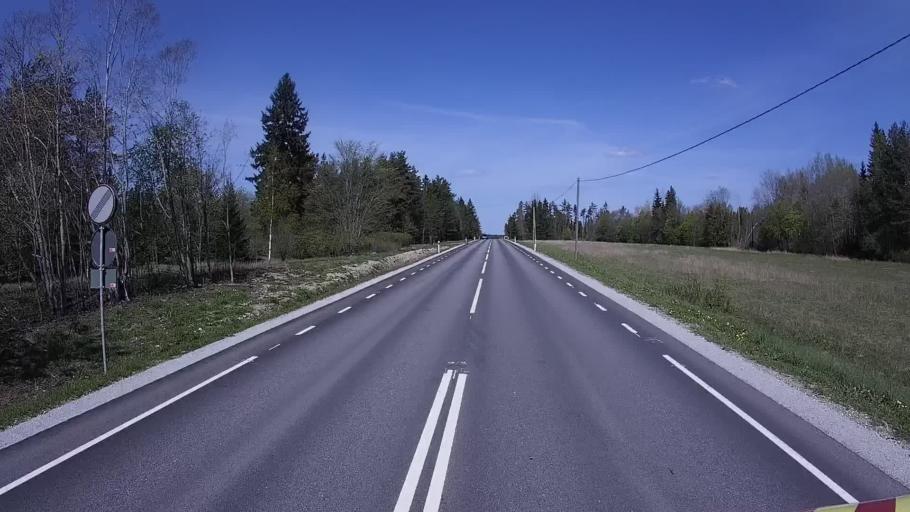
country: EE
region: Harju
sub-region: Paldiski linn
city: Paldiski
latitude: 59.2014
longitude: 24.0968
